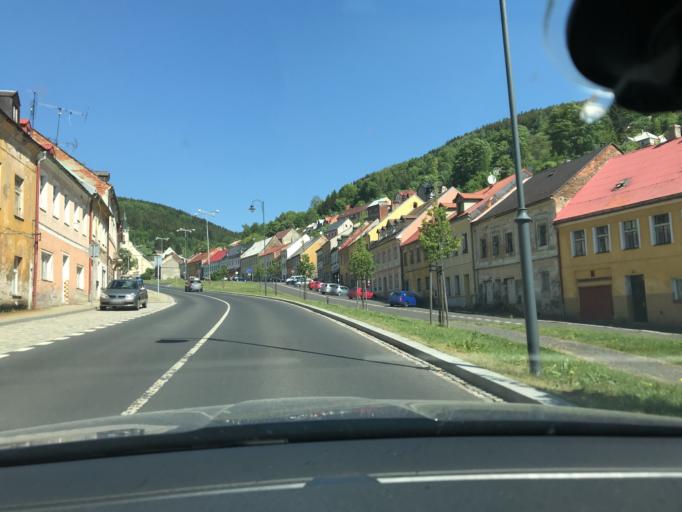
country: CZ
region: Karlovarsky
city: Jachymov
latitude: 50.3685
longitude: 12.9175
